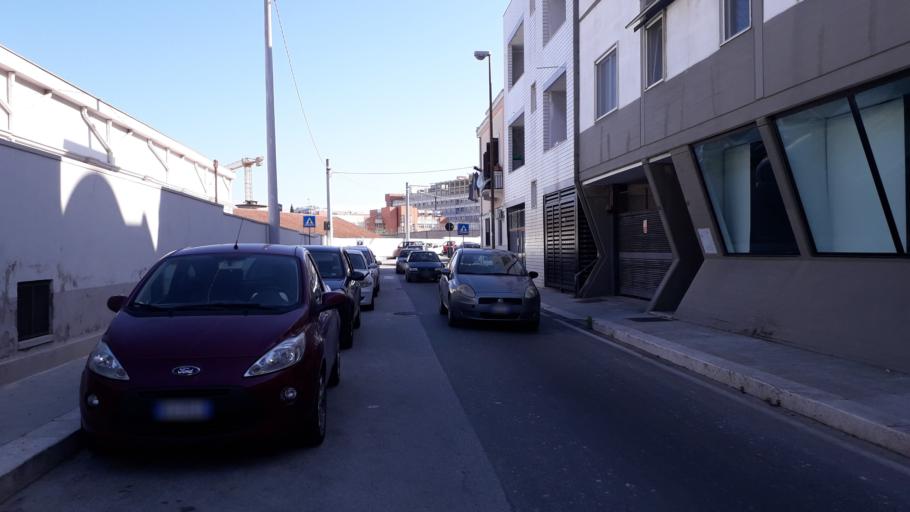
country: IT
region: Apulia
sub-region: Provincia di Bari
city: Bari
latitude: 41.1140
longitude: 16.8547
